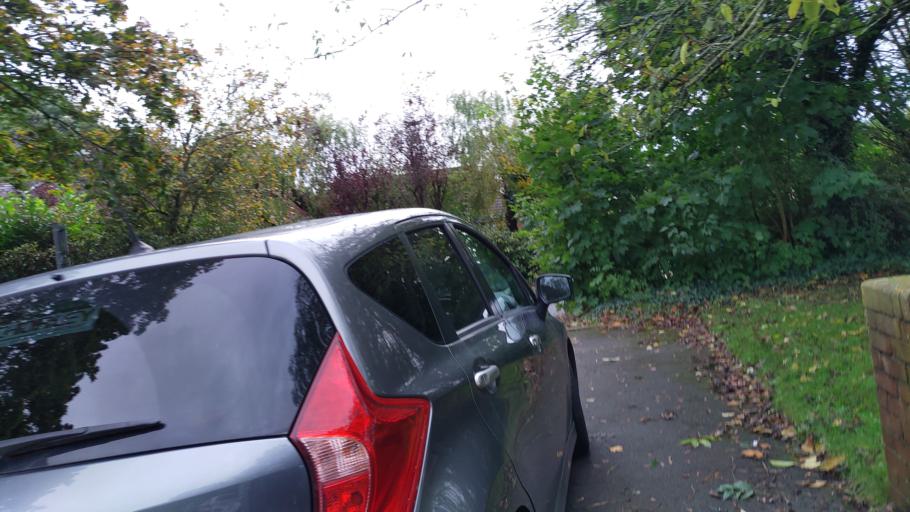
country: GB
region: England
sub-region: Lancashire
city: Euxton
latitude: 53.6606
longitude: -2.6478
